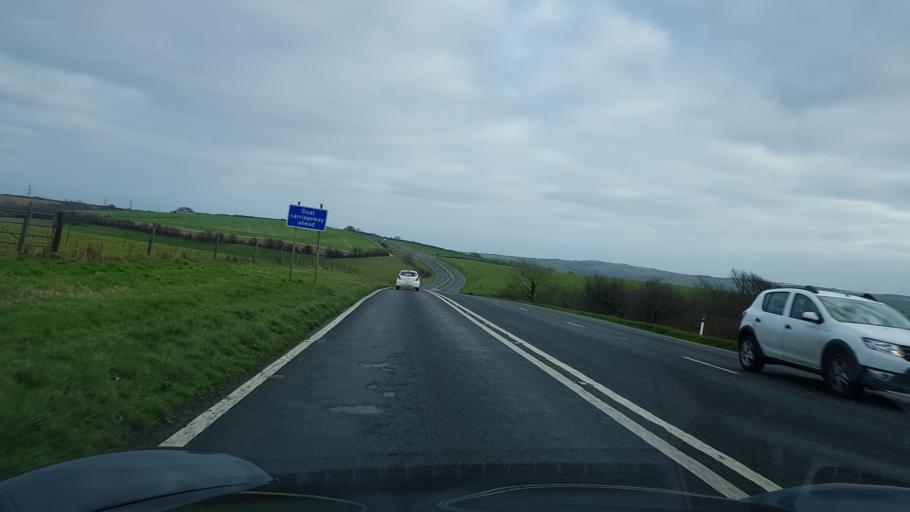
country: GB
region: England
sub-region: Dorset
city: Bridport
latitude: 50.7254
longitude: -2.6521
